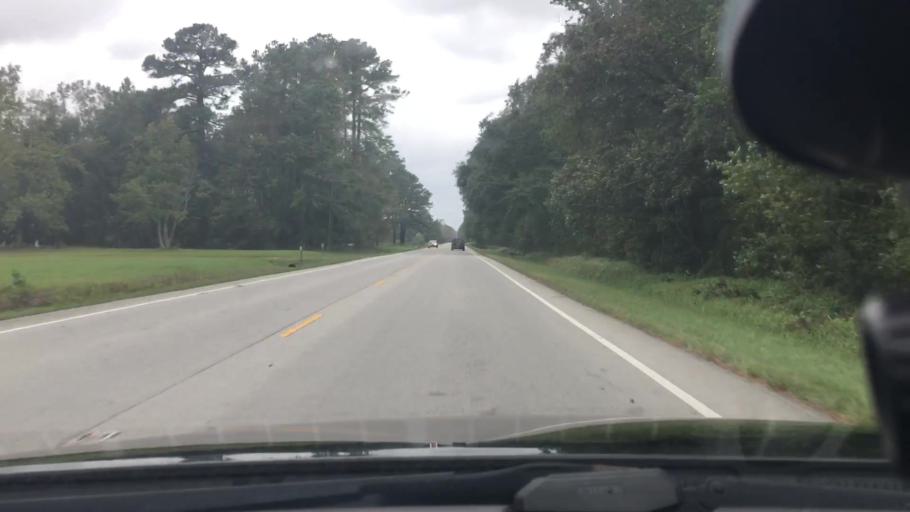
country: US
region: North Carolina
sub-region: Craven County
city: New Bern
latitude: 35.1675
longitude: -77.0416
